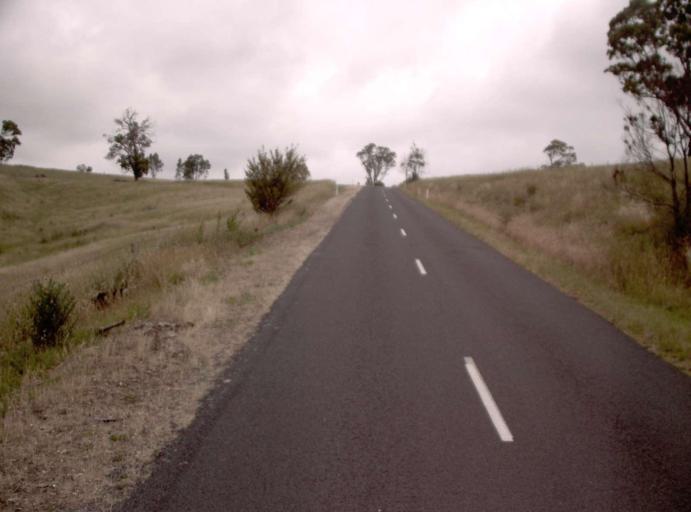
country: AU
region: Victoria
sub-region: Wellington
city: Heyfield
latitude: -37.8787
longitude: 146.7175
